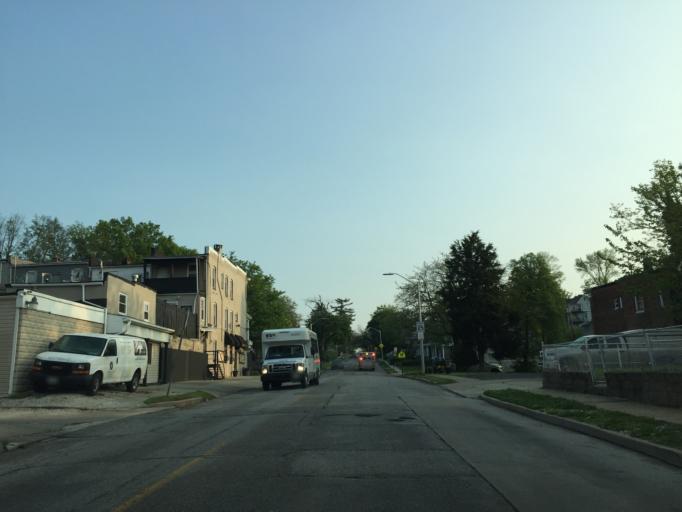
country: US
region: Maryland
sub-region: Baltimore County
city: Lochearn
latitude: 39.3156
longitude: -76.6727
